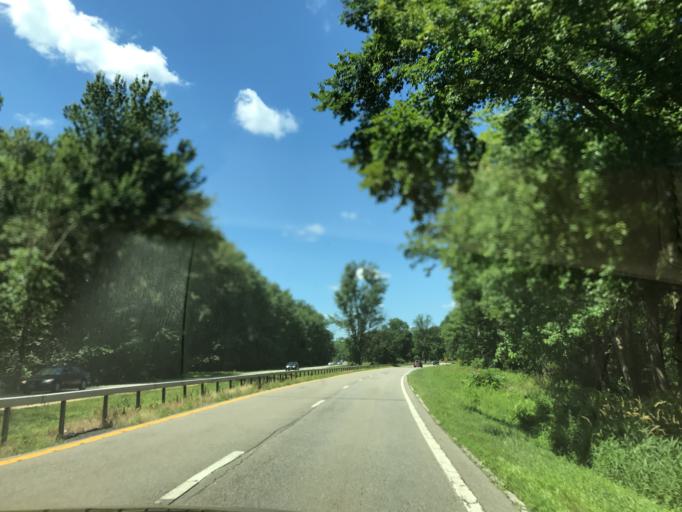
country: US
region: New York
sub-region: Dutchess County
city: Hillside Lake
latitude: 41.5844
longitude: -73.7707
